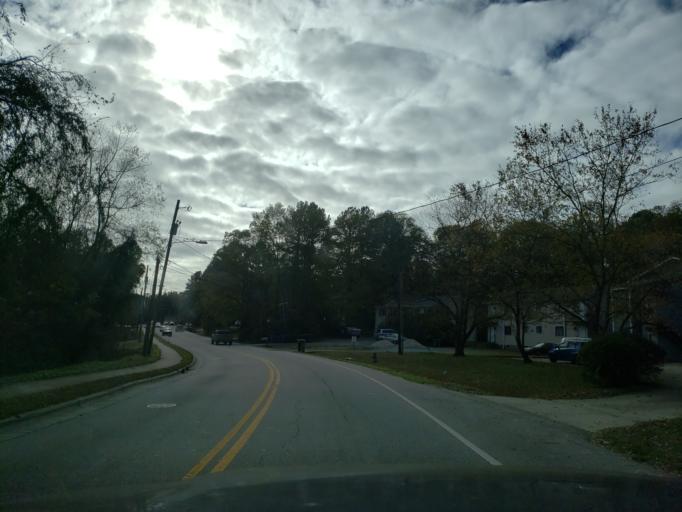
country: US
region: North Carolina
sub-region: Durham County
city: Durham
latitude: 35.9733
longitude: -78.9135
